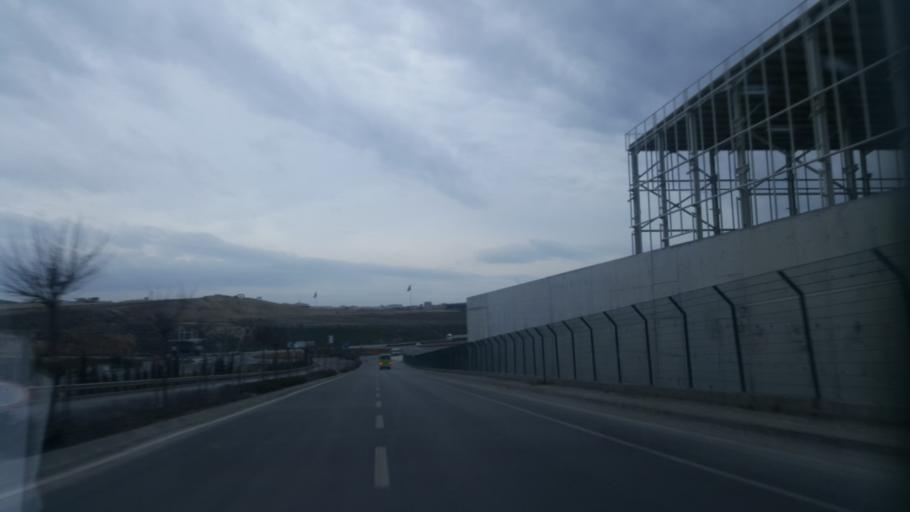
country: TR
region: Kocaeli
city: Tavsanli
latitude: 40.8250
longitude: 29.5594
